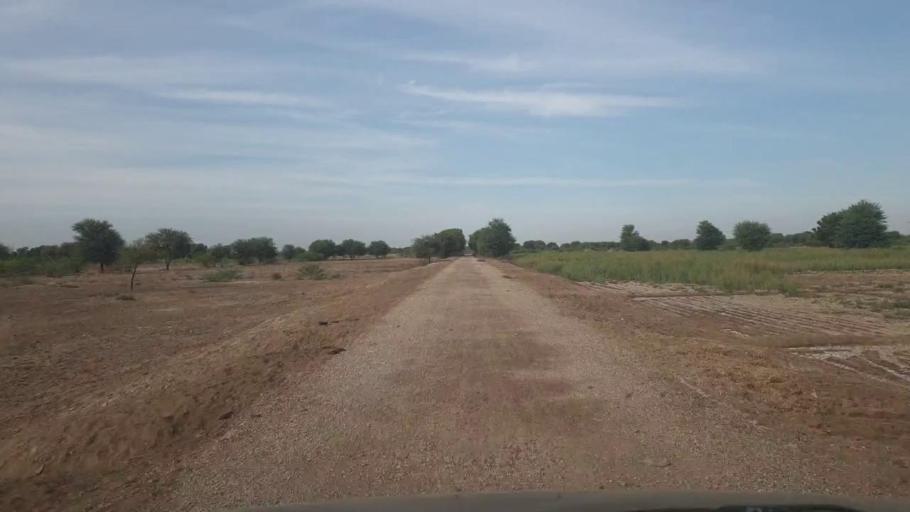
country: PK
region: Sindh
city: Kunri
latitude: 25.2909
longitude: 69.5825
